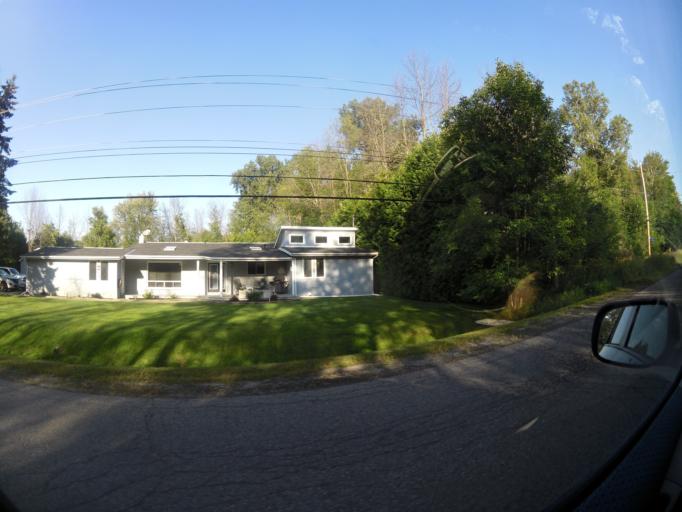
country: CA
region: Ontario
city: Clarence-Rockland
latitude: 45.5114
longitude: -75.4560
